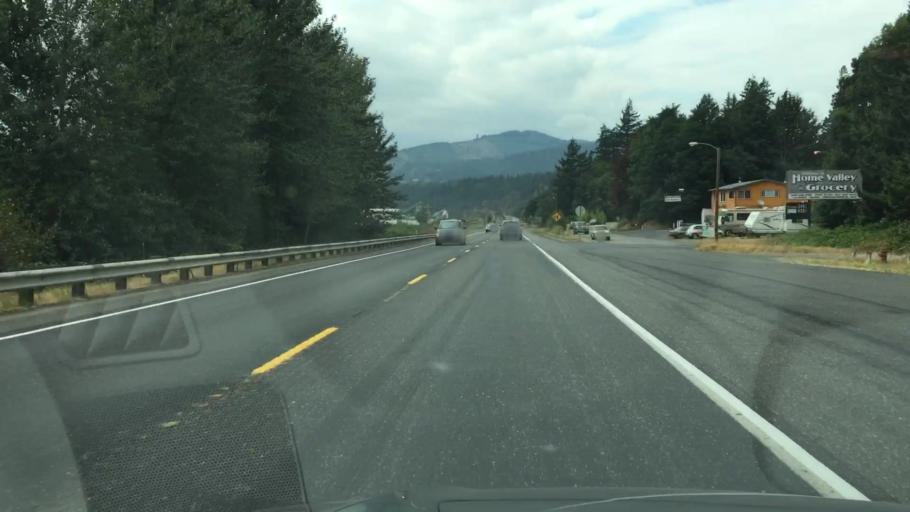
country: US
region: Washington
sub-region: Skamania County
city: Carson
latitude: 45.7105
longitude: -121.7750
